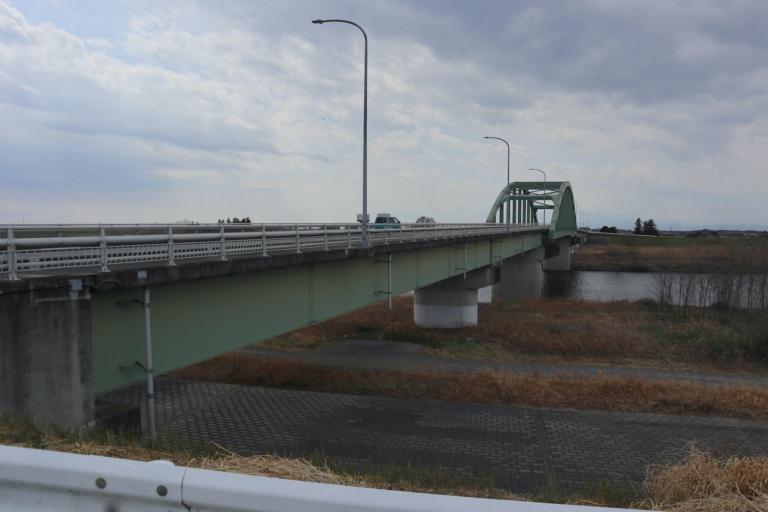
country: JP
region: Gunma
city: Tatebayashi
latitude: 36.2837
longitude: 139.5362
